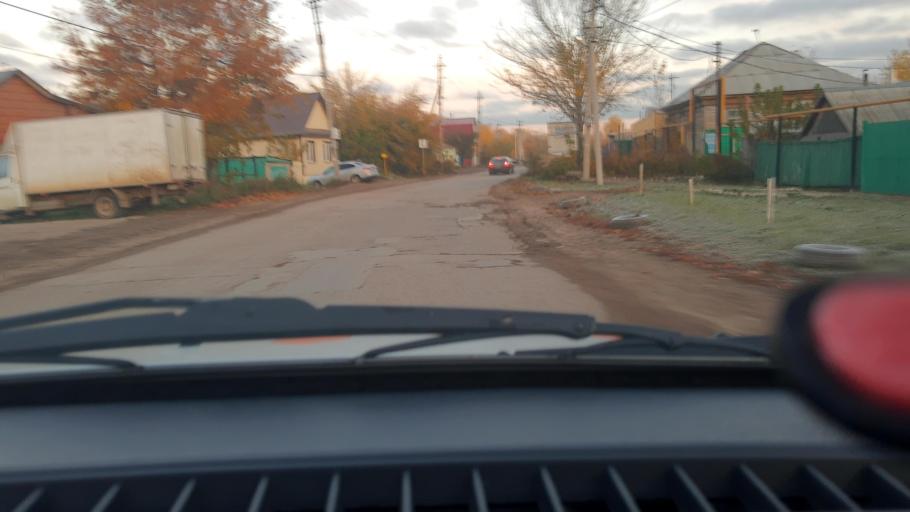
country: RU
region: Bashkortostan
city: Mikhaylovka
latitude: 54.7491
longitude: 55.9089
